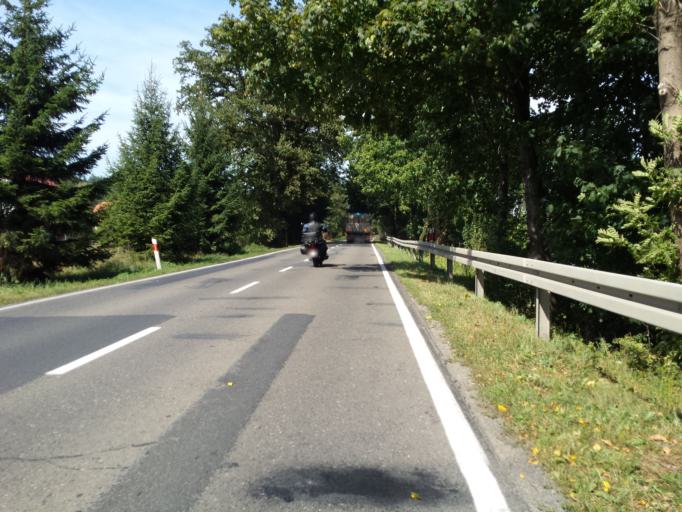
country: PL
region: Subcarpathian Voivodeship
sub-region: Powiat leski
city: Lesko
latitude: 49.4595
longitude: 22.3353
